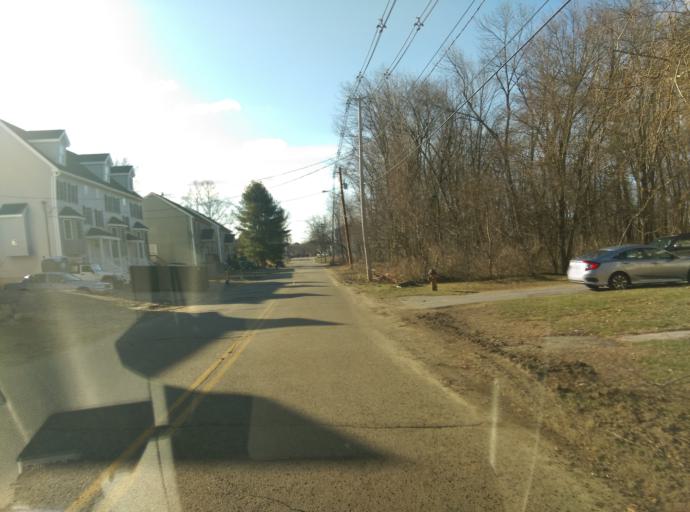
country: US
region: Massachusetts
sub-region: Essex County
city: Haverhill
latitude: 42.7472
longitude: -71.1124
